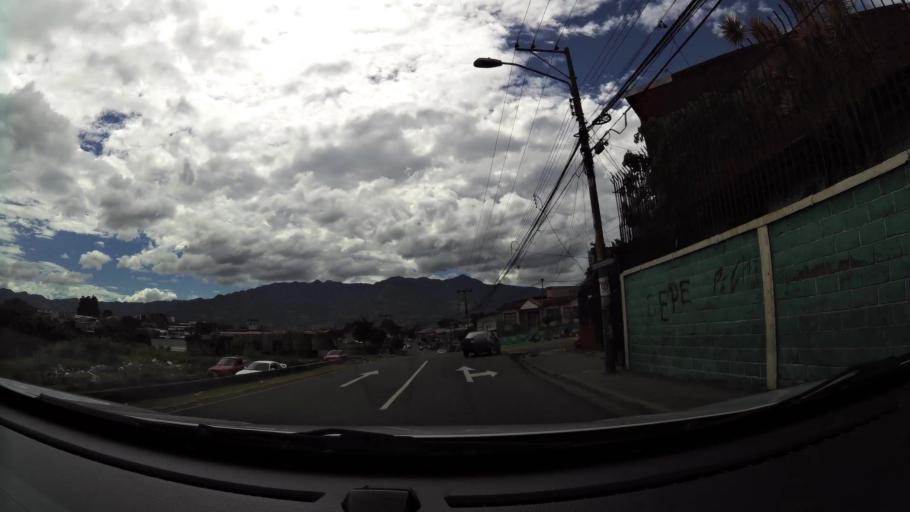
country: CR
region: San Jose
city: San Jose
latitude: 9.9213
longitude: -84.0817
